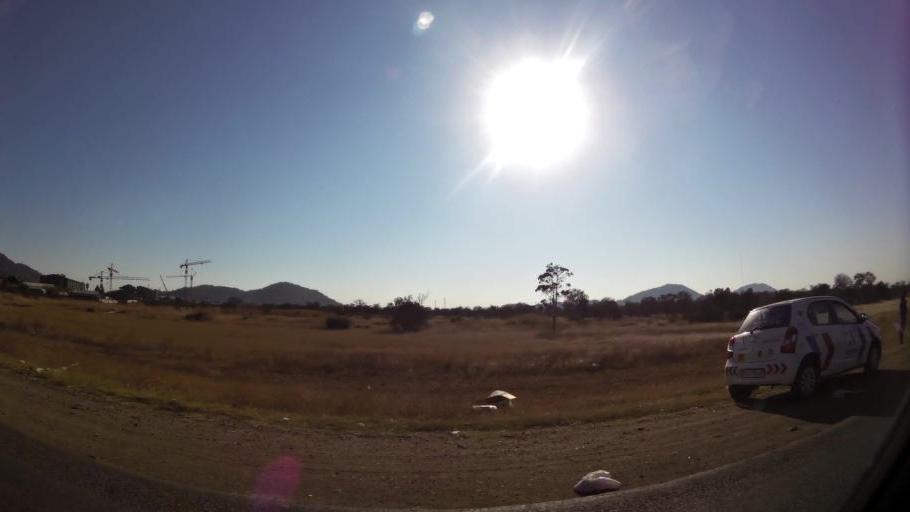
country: ZA
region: Gauteng
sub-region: City of Tshwane Metropolitan Municipality
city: Pretoria
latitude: -25.6372
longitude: 28.1335
